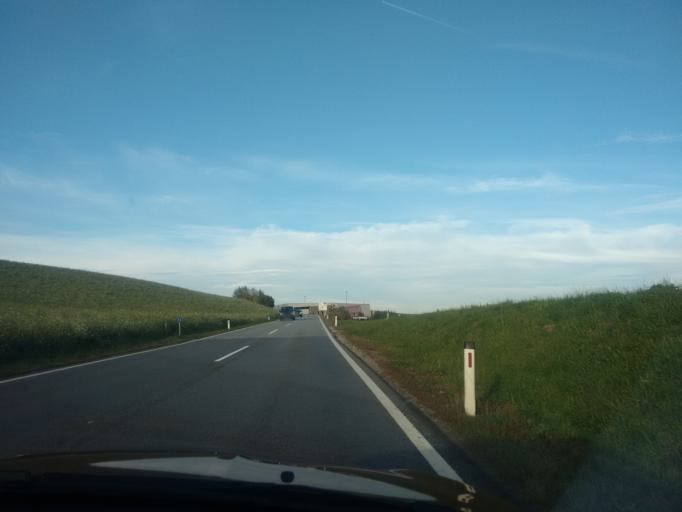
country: AT
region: Upper Austria
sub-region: Wels-Land
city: Offenhausen
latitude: 48.1806
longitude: 13.7789
